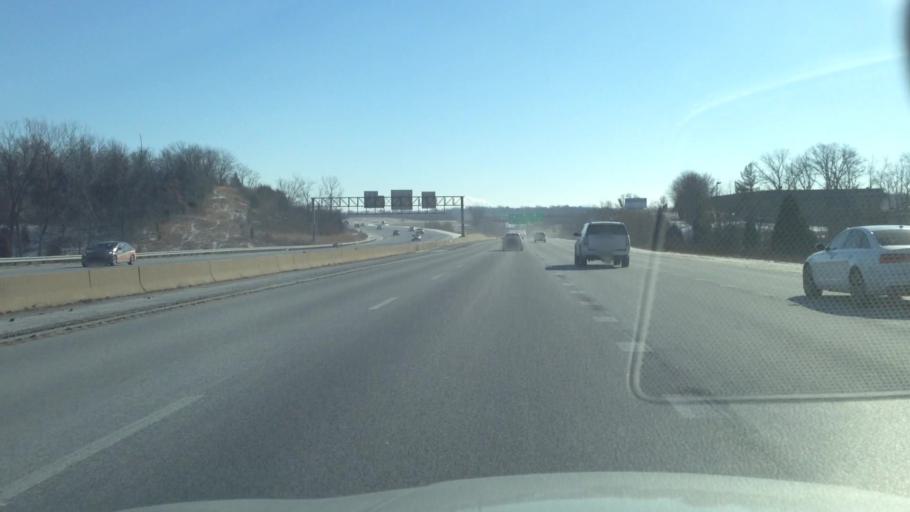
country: US
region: Missouri
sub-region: Platte County
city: Riverside
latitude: 39.1869
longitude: -94.6004
